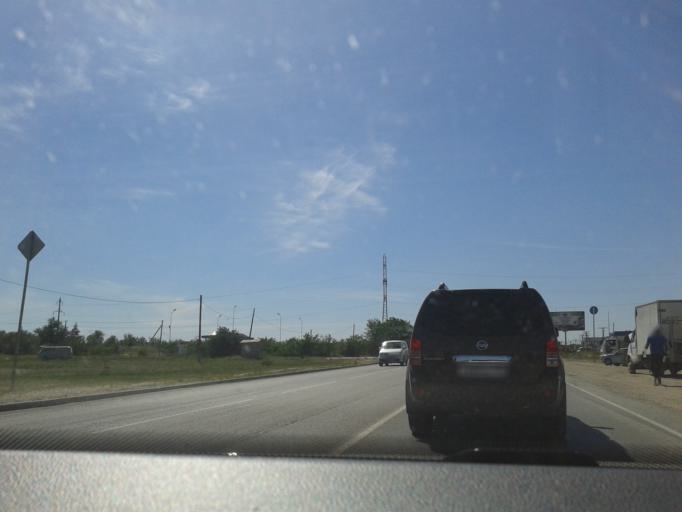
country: RU
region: Volgograd
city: Volgograd
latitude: 48.7044
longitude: 44.4456
